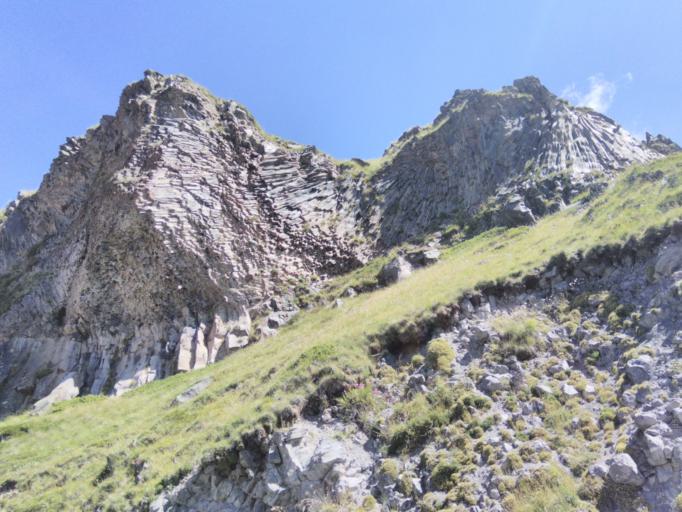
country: RU
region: Kabardino-Balkariya
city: Terskol
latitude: 43.2685
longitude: 42.4947
